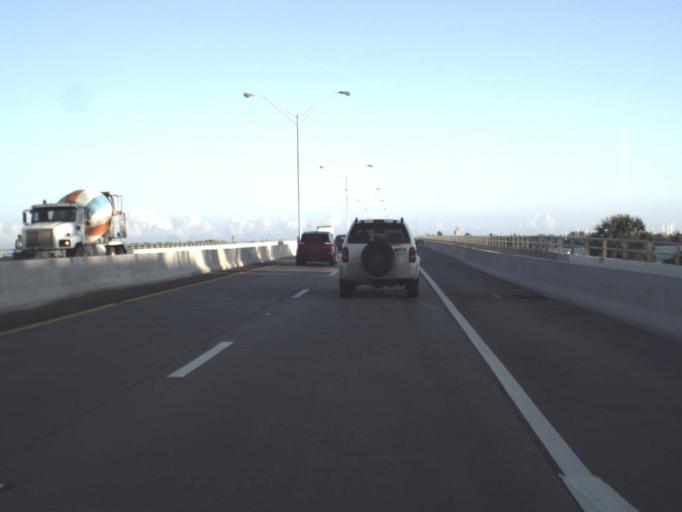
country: US
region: Florida
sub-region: Miami-Dade County
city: Key Biscayne
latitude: 25.7328
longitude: -80.1615
